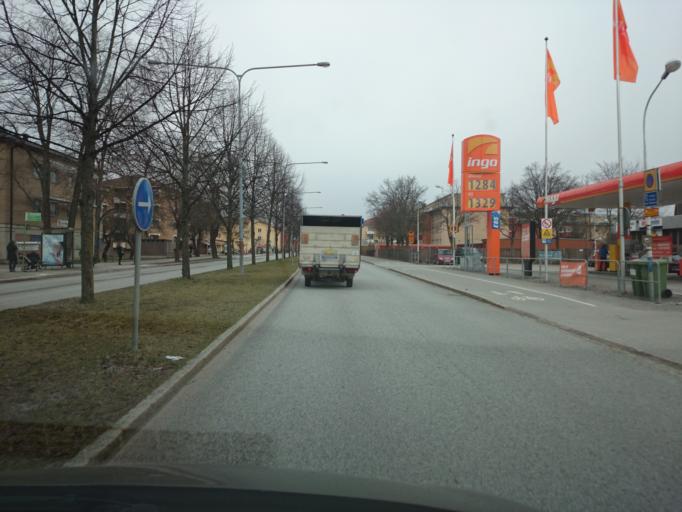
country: SE
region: Uppsala
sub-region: Uppsala Kommun
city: Uppsala
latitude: 59.8688
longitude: 17.6284
